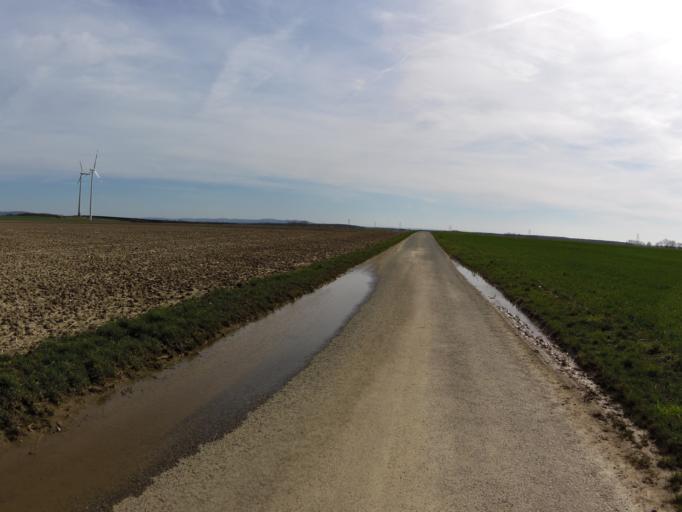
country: DE
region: Bavaria
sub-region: Regierungsbezirk Unterfranken
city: Biebelried
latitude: 49.7573
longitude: 10.0861
